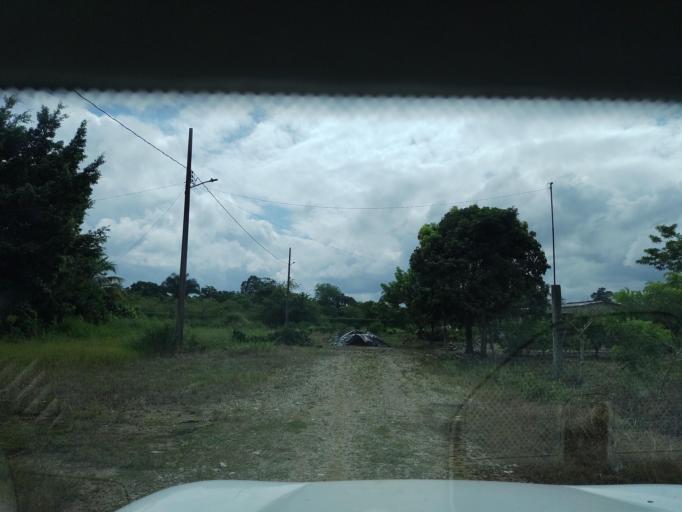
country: MX
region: Veracruz
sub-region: Atzalan
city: Colonias Pedernales
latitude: 20.0379
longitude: -97.0717
